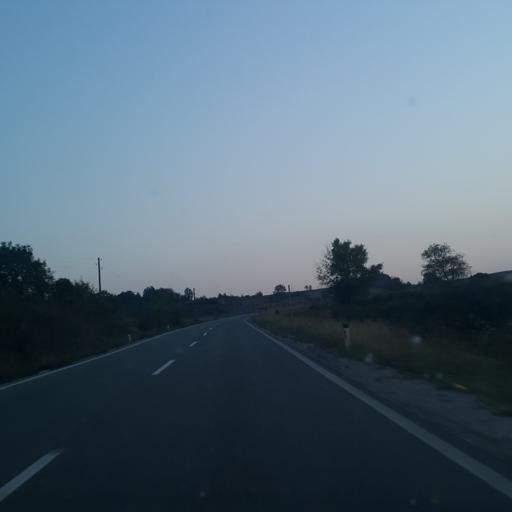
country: RS
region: Central Serbia
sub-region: Nisavski Okrug
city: Svrljig
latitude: 43.4349
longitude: 22.1622
